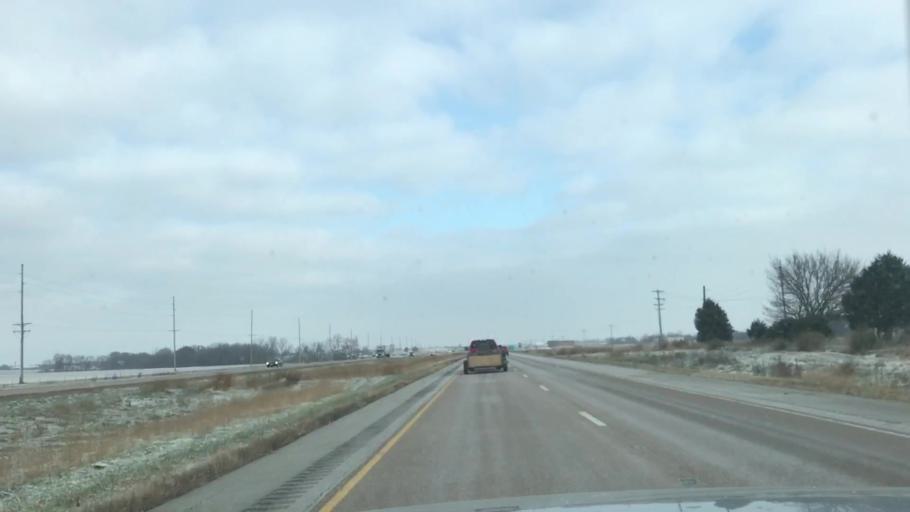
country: US
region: Illinois
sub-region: Macoupin County
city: Staunton
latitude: 39.0052
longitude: -89.7496
